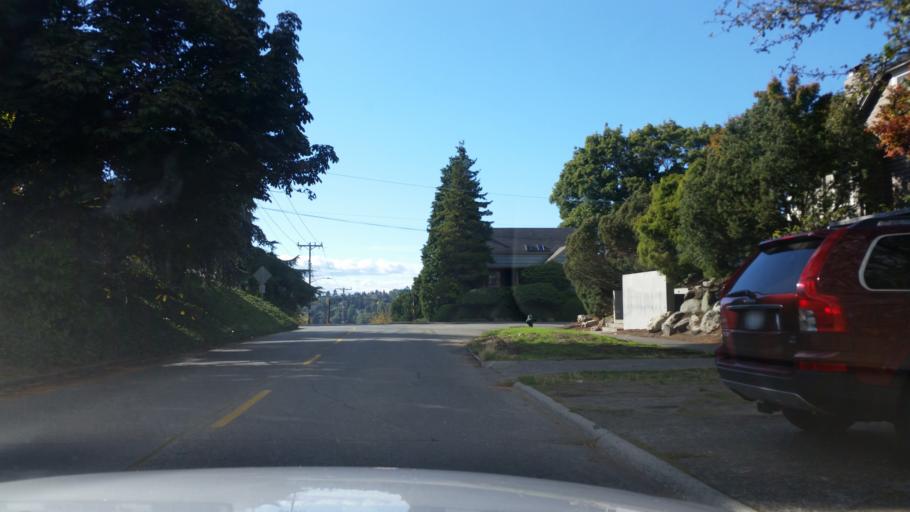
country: US
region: Washington
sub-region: King County
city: Seattle
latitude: 47.6469
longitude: -122.3698
